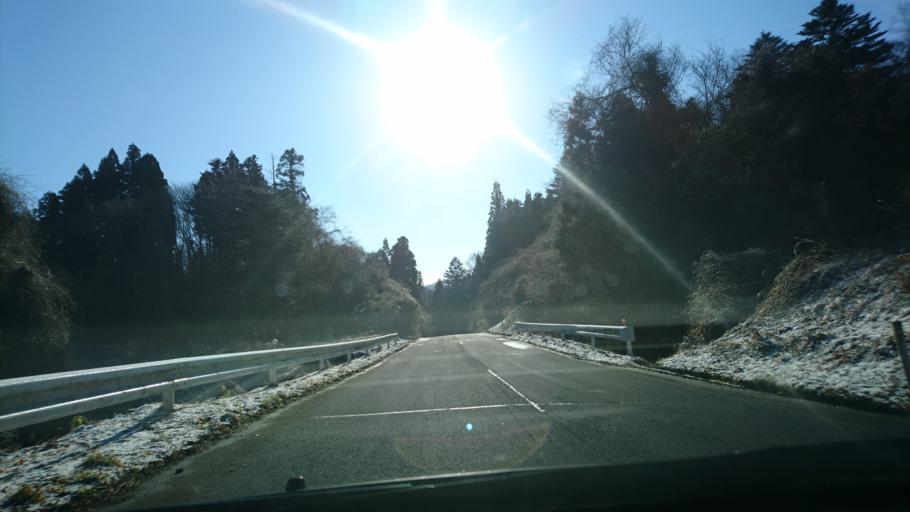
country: JP
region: Iwate
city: Ichinoseki
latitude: 38.8770
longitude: 141.3281
